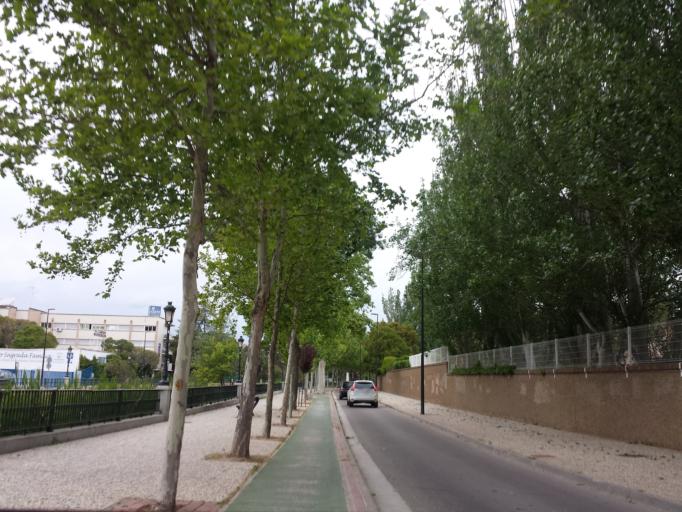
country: ES
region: Aragon
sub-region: Provincia de Zaragoza
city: Delicias
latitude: 41.6229
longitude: -0.9054
